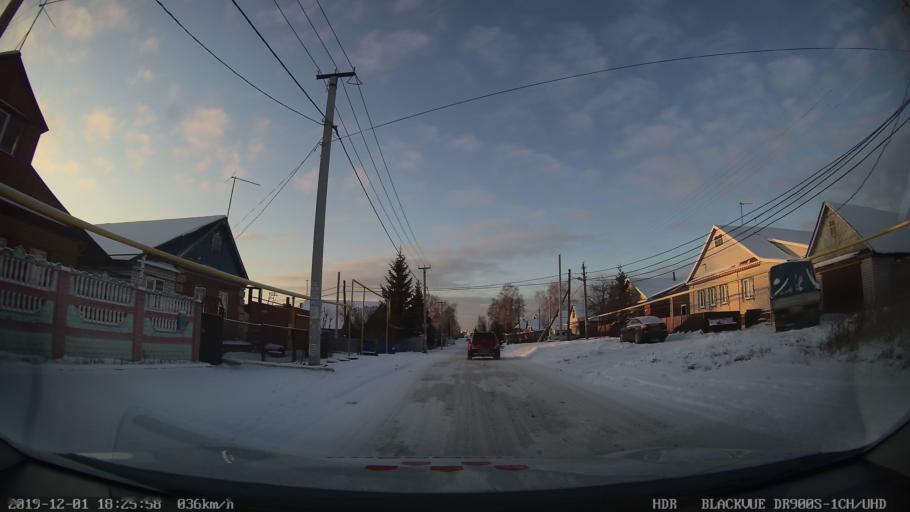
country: RU
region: Tatarstan
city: Vysokaya Gora
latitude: 55.8096
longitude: 49.2597
